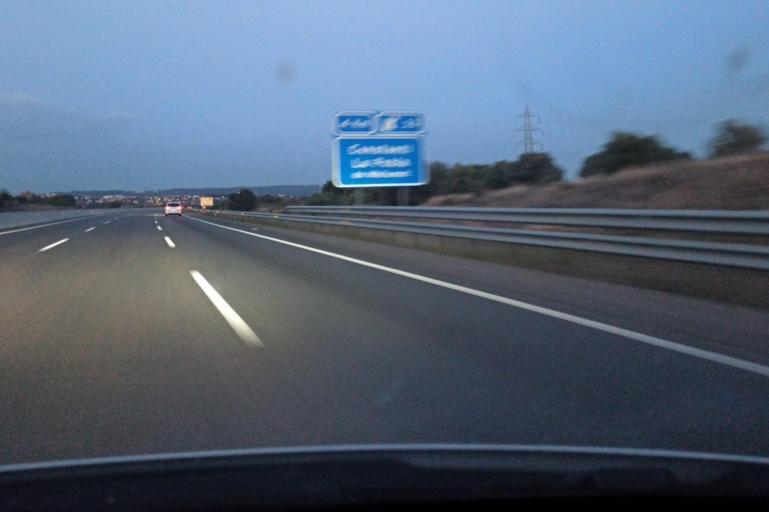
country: ES
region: Catalonia
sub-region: Provincia de Tarragona
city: Constanti
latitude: 41.1427
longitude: 1.1929
